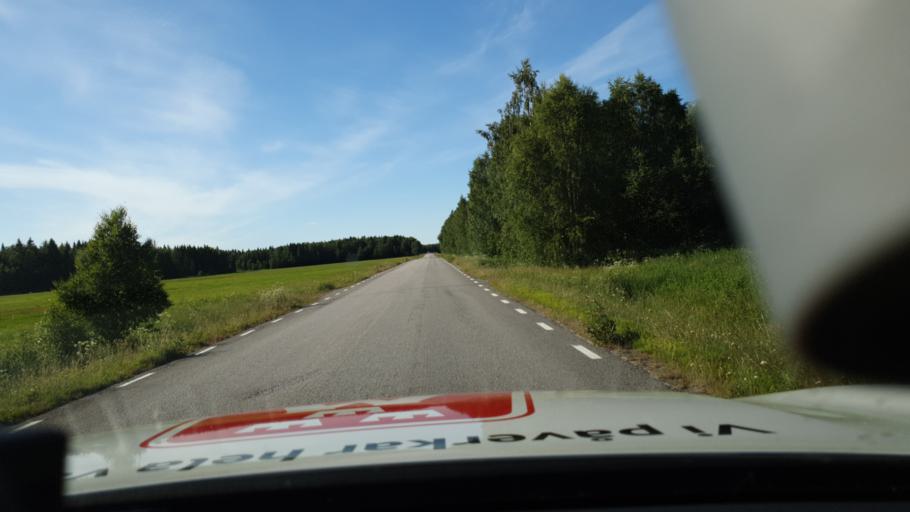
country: SE
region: Norrbotten
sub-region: Kalix Kommun
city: Toere
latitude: 65.8738
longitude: 22.6727
